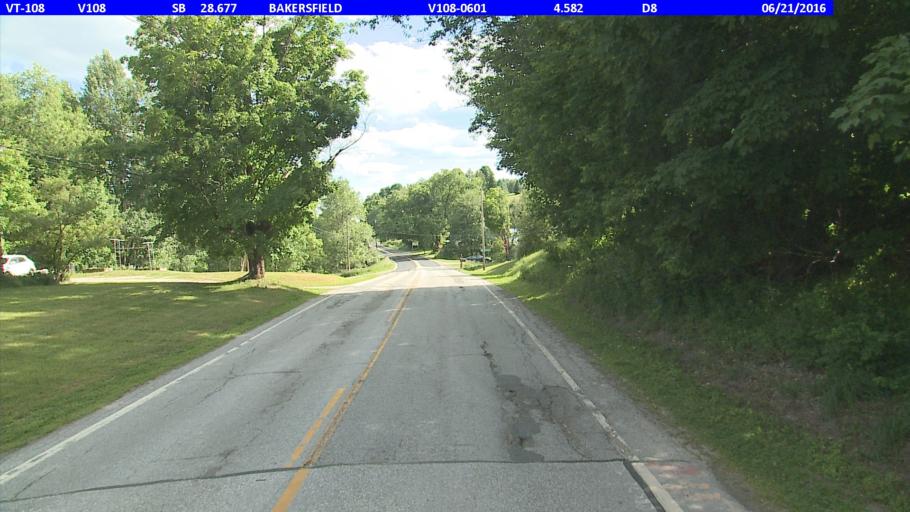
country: US
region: Vermont
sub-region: Franklin County
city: Enosburg Falls
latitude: 44.7948
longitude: -72.7968
